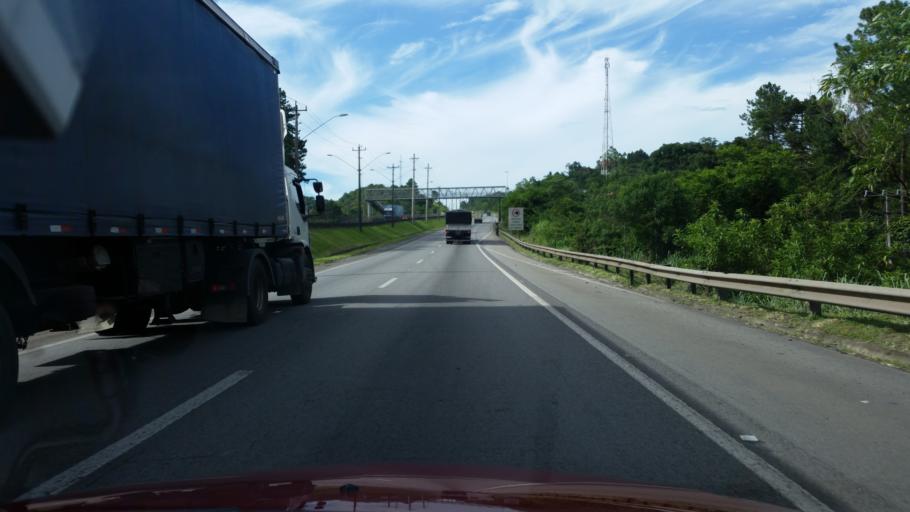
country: BR
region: Sao Paulo
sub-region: Sao Lourenco Da Serra
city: Sao Lourenco da Serra
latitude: -23.8171
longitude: -46.9241
